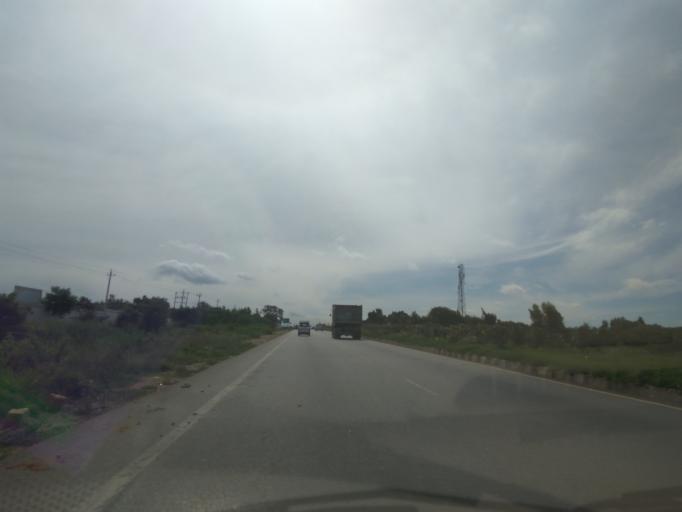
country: IN
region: Karnataka
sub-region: Bangalore Rural
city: Dasarahalli
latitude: 13.1318
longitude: 77.9544
